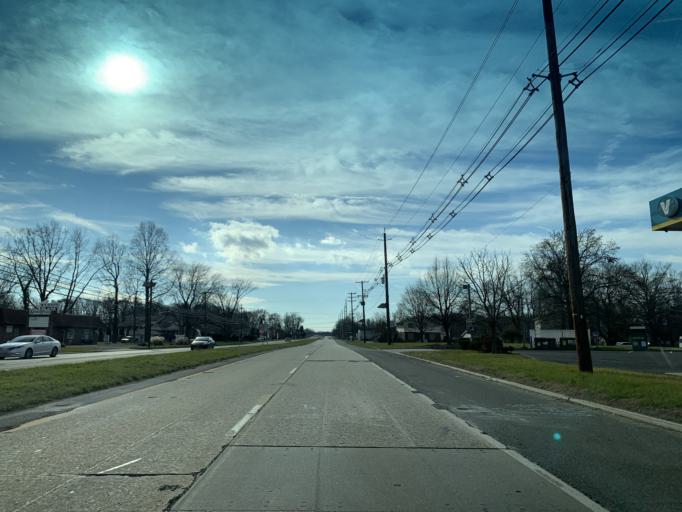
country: US
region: New Jersey
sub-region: Mercer County
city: Groveville
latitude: 40.1673
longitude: -74.6876
